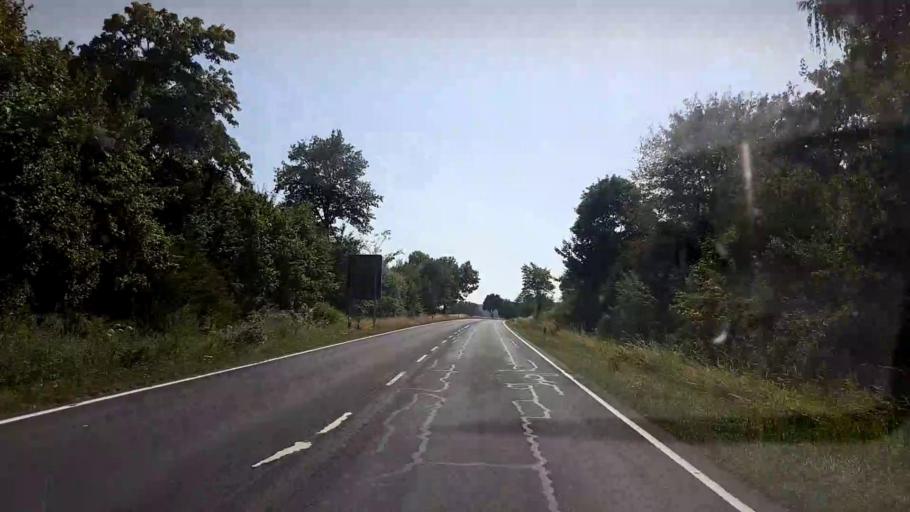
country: DE
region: Bavaria
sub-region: Regierungsbezirk Unterfranken
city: Untermerzbach
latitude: 50.1255
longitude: 10.8821
